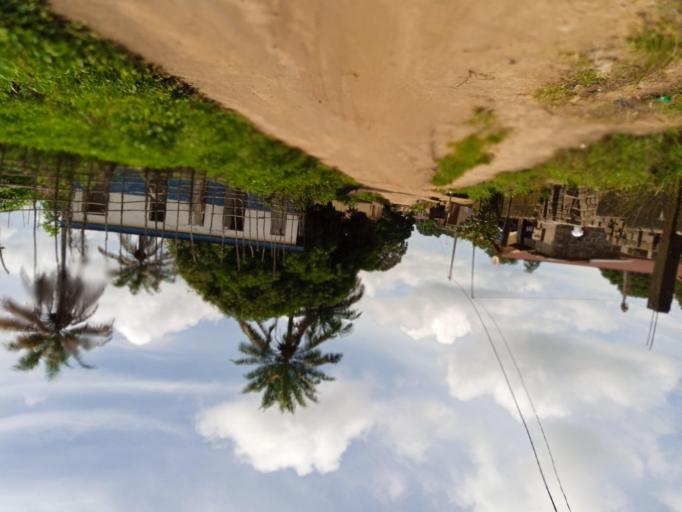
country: SL
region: Northern Province
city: Masoyila
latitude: 8.6069
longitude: -13.1873
